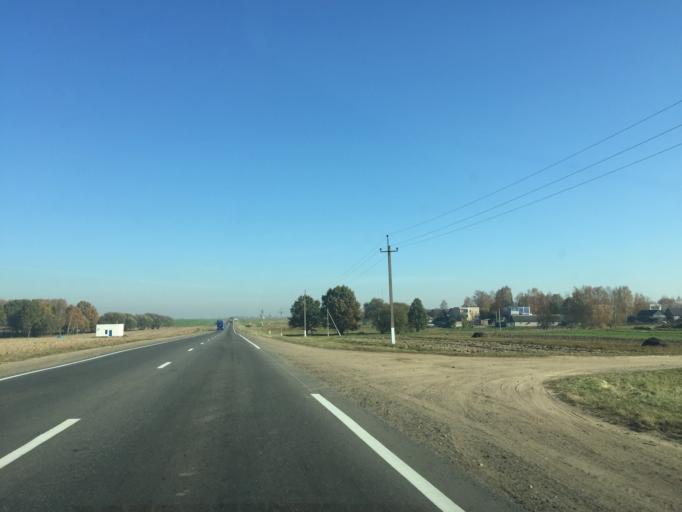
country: BY
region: Mogilev
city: Buynichy
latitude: 53.9565
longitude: 30.2355
